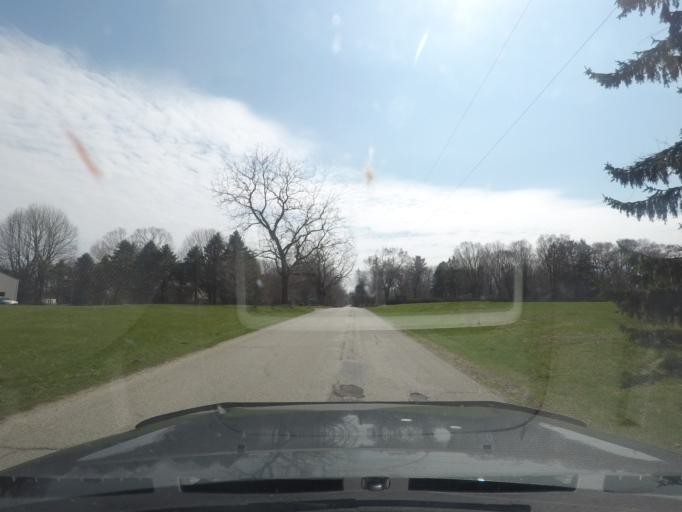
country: US
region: Indiana
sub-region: LaPorte County
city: Westville
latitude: 41.5231
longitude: -86.7989
